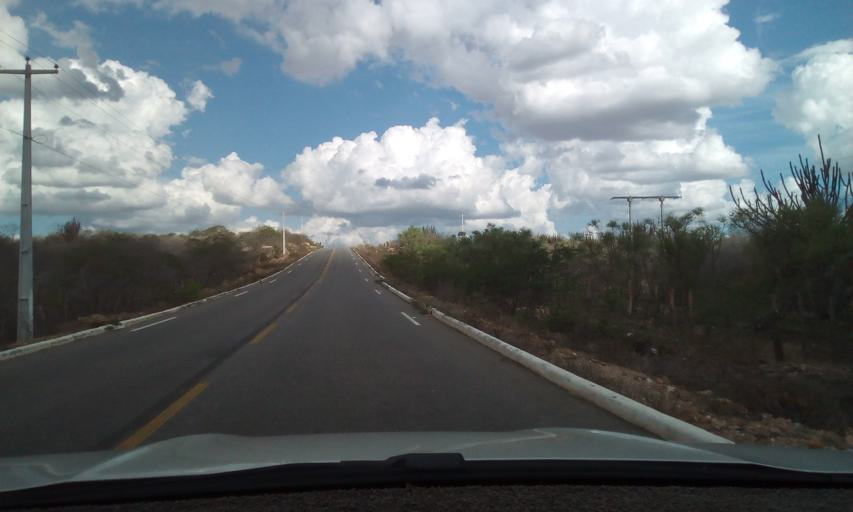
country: BR
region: Rio Grande do Norte
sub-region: Parelhas
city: Parelhas
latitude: -6.7942
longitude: -36.4198
